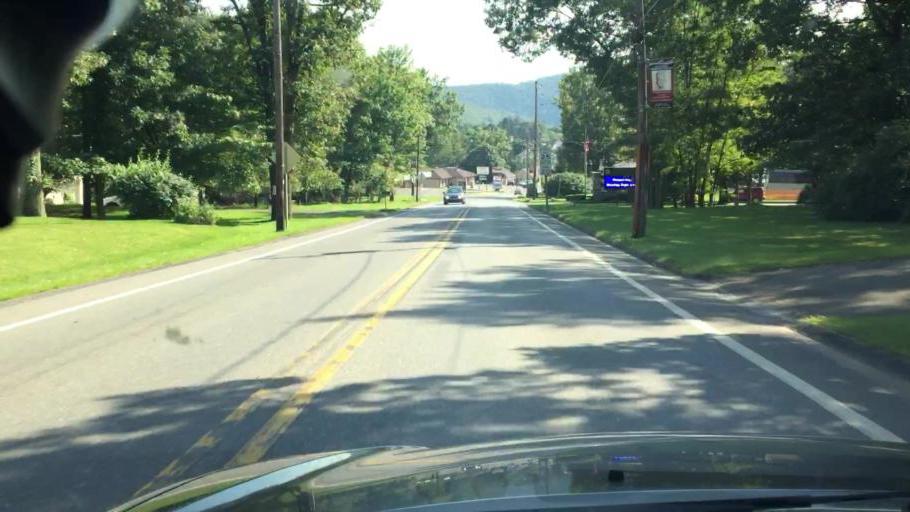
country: US
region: Pennsylvania
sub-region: Carbon County
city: Jim Thorpe
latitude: 40.8838
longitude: -75.7255
